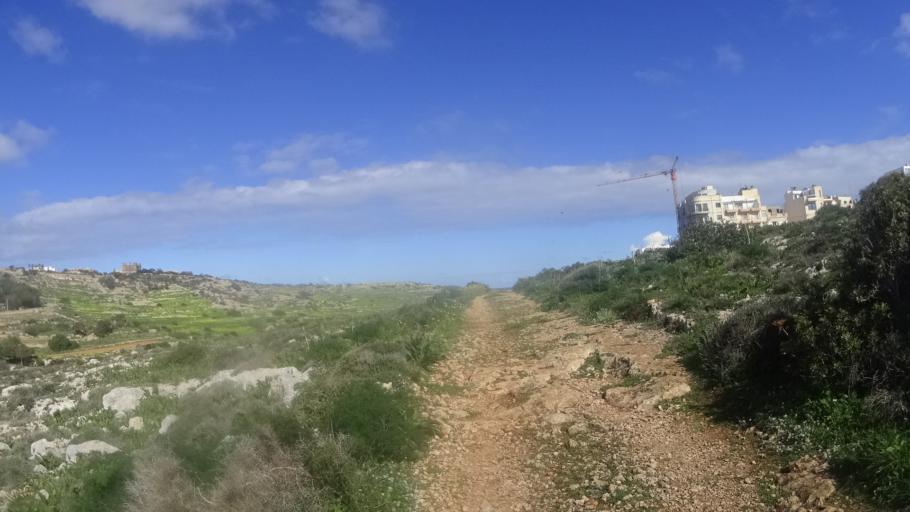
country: MT
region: Il-Mellieha
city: Mellieha
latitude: 35.9508
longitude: 14.3804
